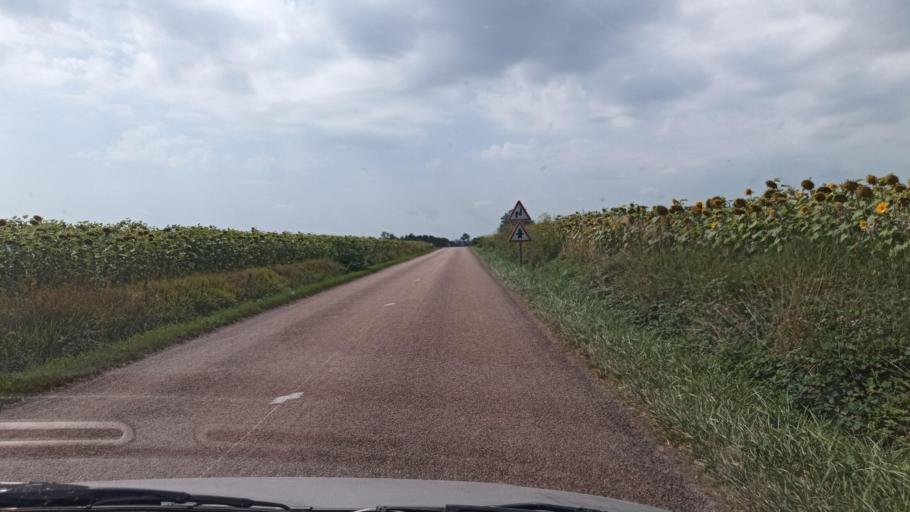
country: FR
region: Bourgogne
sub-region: Departement de l'Yonne
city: Egriselles-le-Bocage
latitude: 48.0403
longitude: 3.2012
